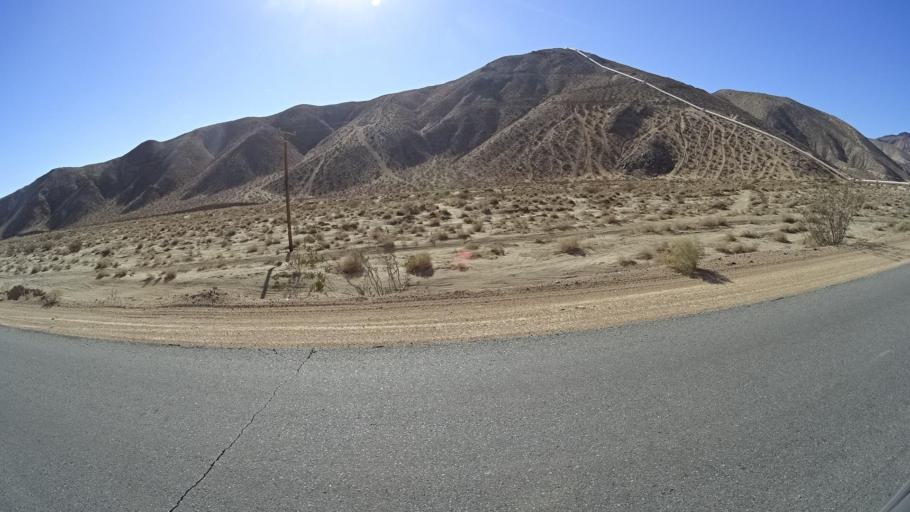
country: US
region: California
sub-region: Kern County
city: California City
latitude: 35.3145
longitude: -118.0413
